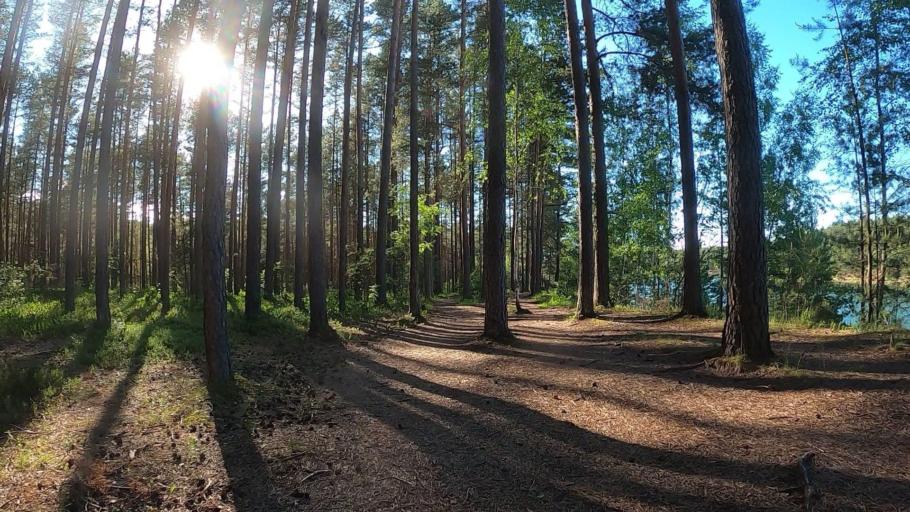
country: LV
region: Ikskile
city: Ikskile
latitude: 56.8368
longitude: 24.5557
